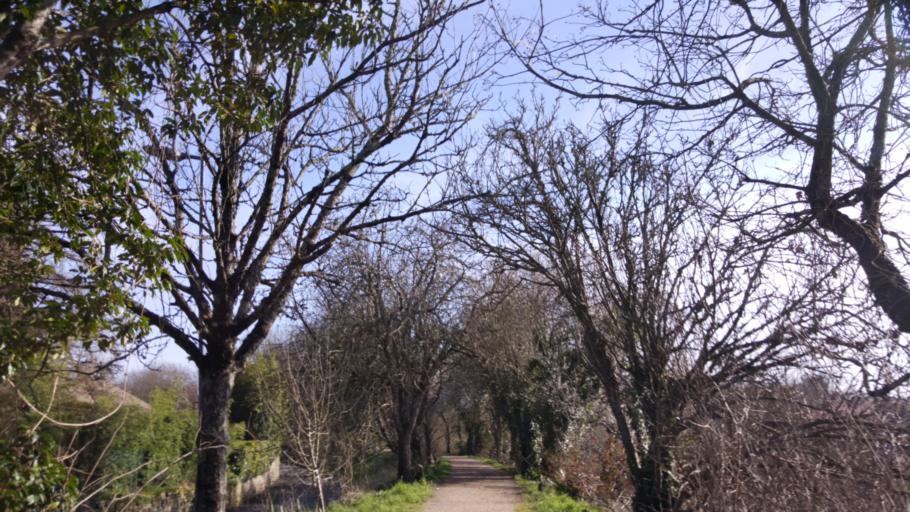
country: FR
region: Poitou-Charentes
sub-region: Departement des Deux-Sevres
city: Melle
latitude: 46.2237
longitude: -0.1394
